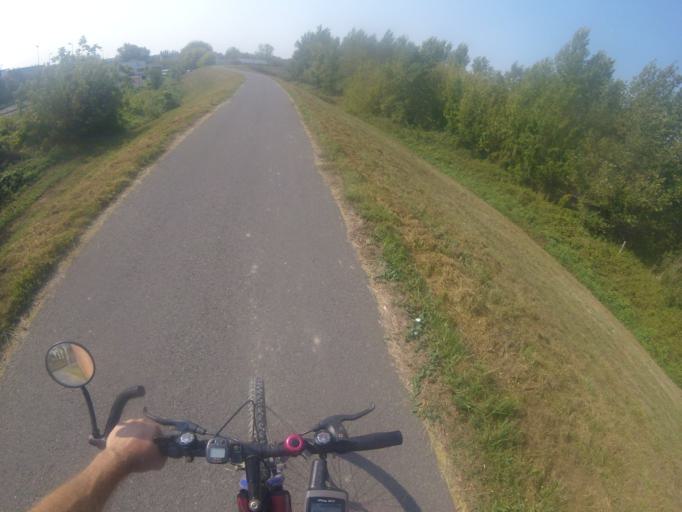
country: HU
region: Bacs-Kiskun
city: Baja
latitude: 46.1915
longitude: 18.9332
